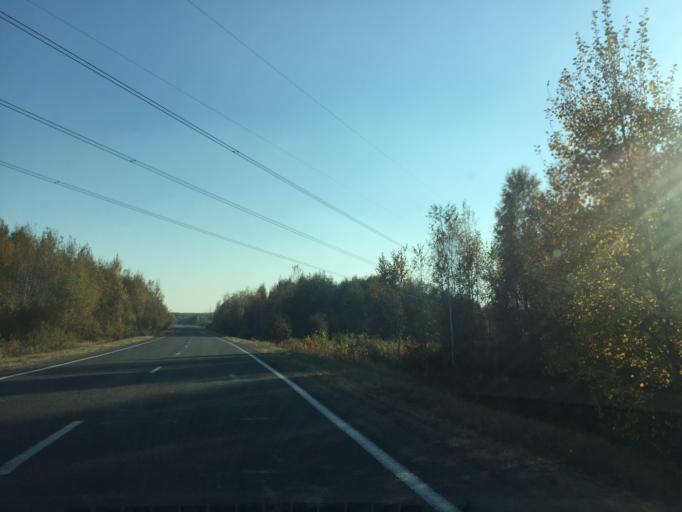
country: BY
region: Gomel
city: Dobrush
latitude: 52.3501
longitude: 31.2292
